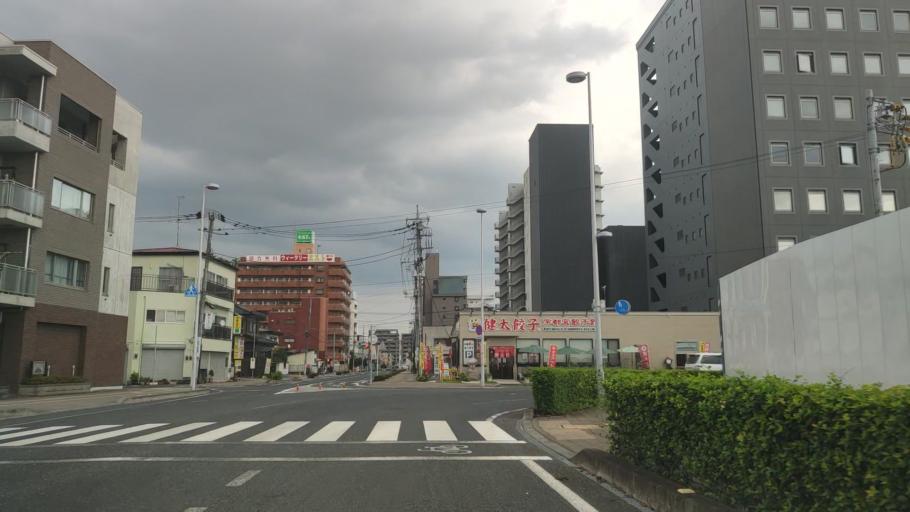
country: JP
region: Tochigi
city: Utsunomiya-shi
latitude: 36.5599
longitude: 139.9008
